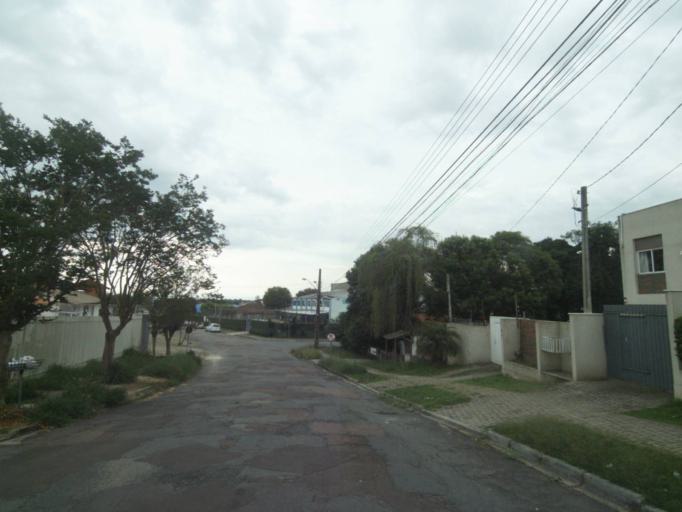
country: BR
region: Parana
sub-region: Curitiba
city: Curitiba
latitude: -25.3971
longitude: -49.2887
